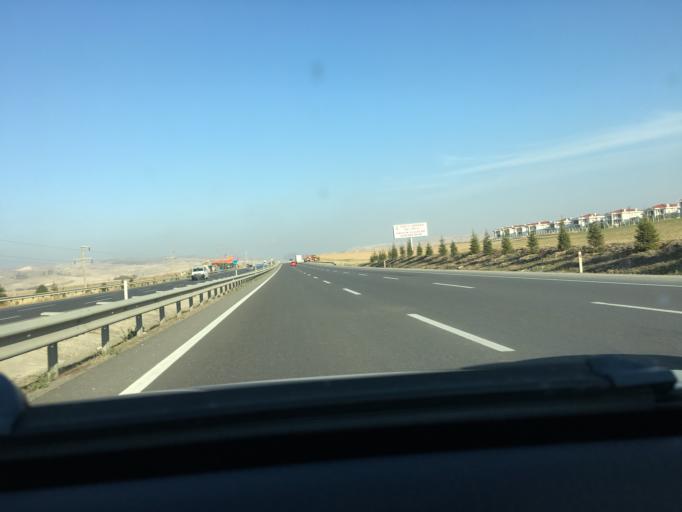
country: TR
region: Ankara
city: Temelli
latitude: 39.7473
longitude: 32.4224
